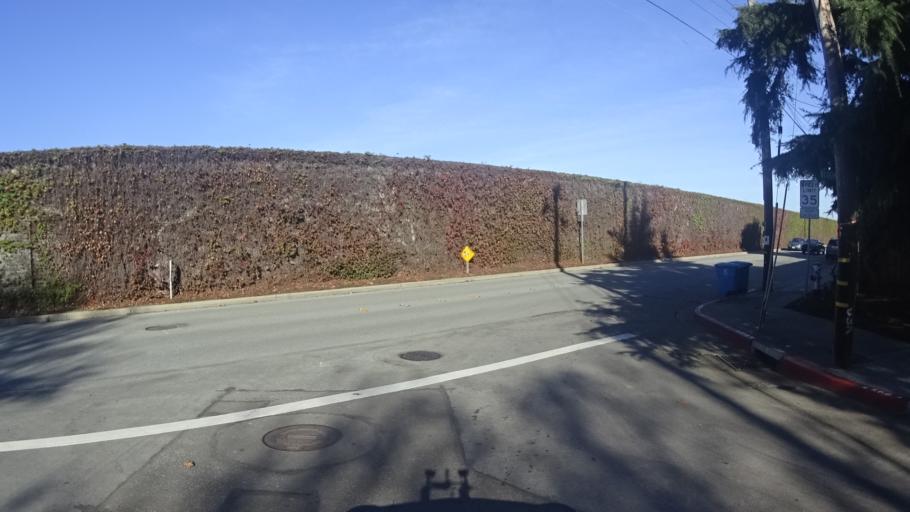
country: US
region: California
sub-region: San Mateo County
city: Burlingame
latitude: 37.5866
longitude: -122.3448
